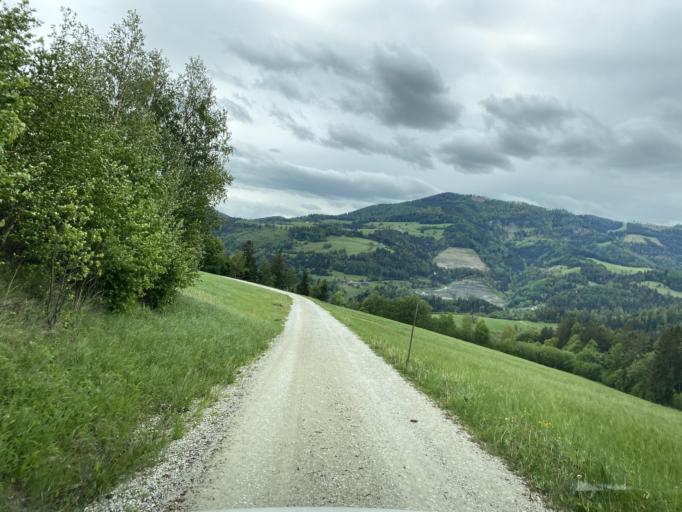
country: AT
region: Styria
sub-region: Politischer Bezirk Weiz
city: Baierdorf-Umgebung
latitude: 47.2999
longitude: 15.7021
